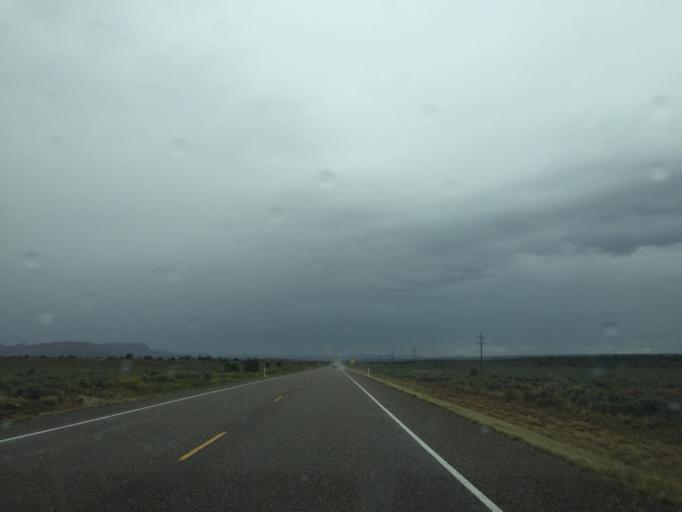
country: US
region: Utah
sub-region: Kane County
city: Kanab
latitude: 37.0936
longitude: -112.1423
